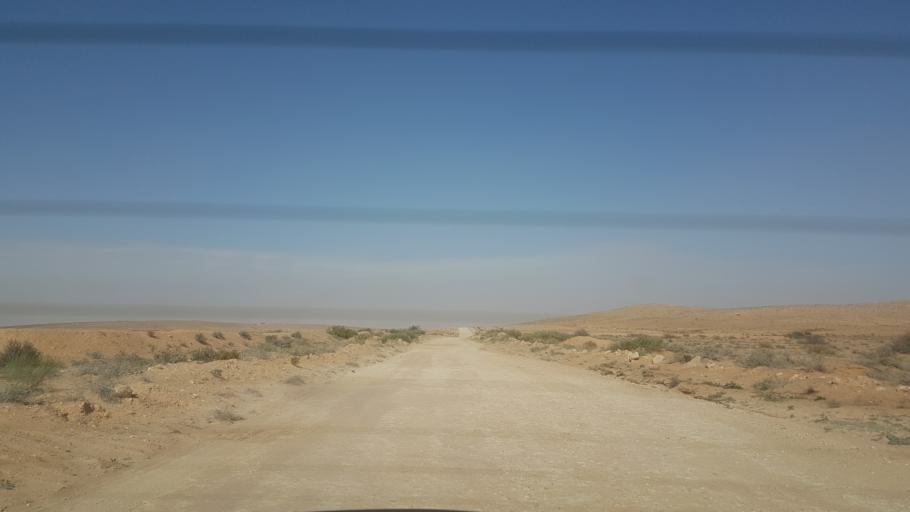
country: TN
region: Qabis
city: El Hamma
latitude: 33.6518
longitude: 9.7364
